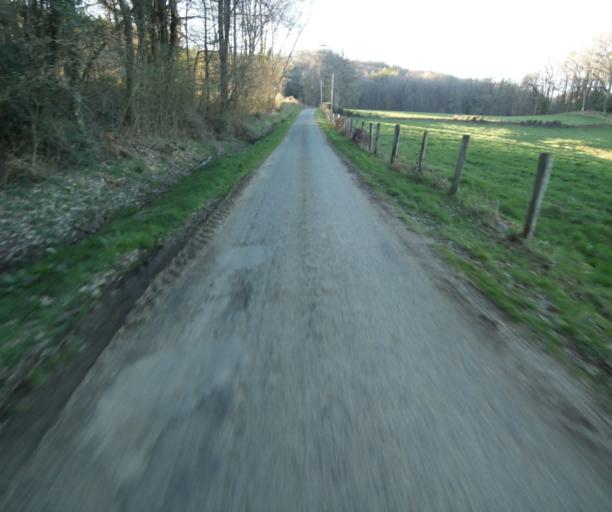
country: FR
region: Limousin
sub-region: Departement de la Correze
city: Seilhac
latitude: 45.3462
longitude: 1.7216
